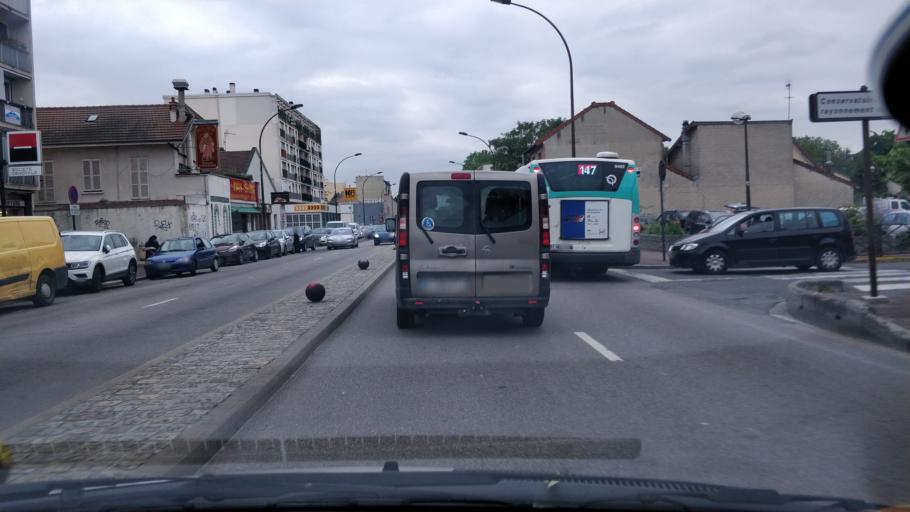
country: FR
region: Ile-de-France
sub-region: Departement de Seine-Saint-Denis
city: Livry-Gargan
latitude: 48.9186
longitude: 2.5365
